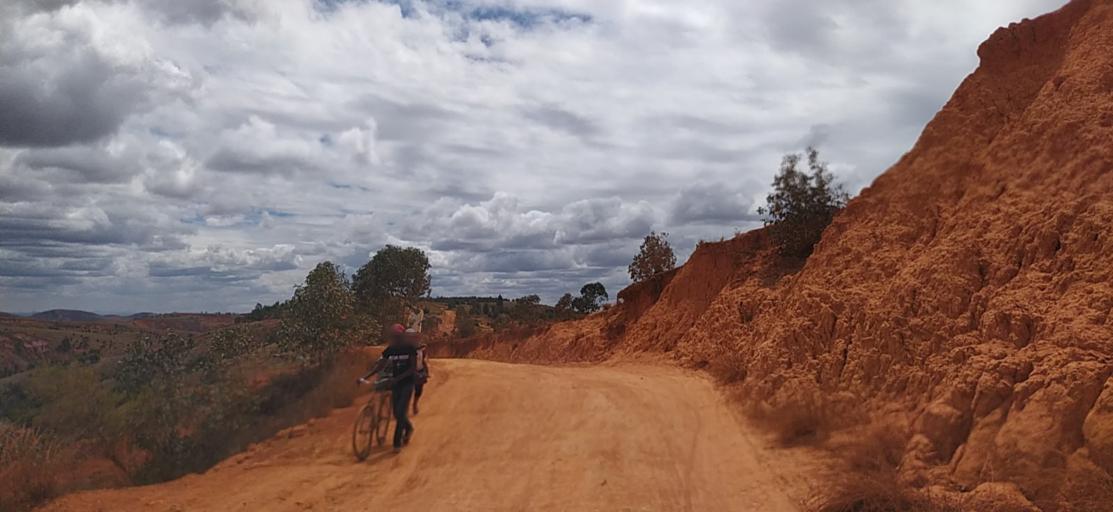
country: MG
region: Alaotra Mangoro
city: Ambatondrazaka
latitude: -18.0602
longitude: 48.2568
